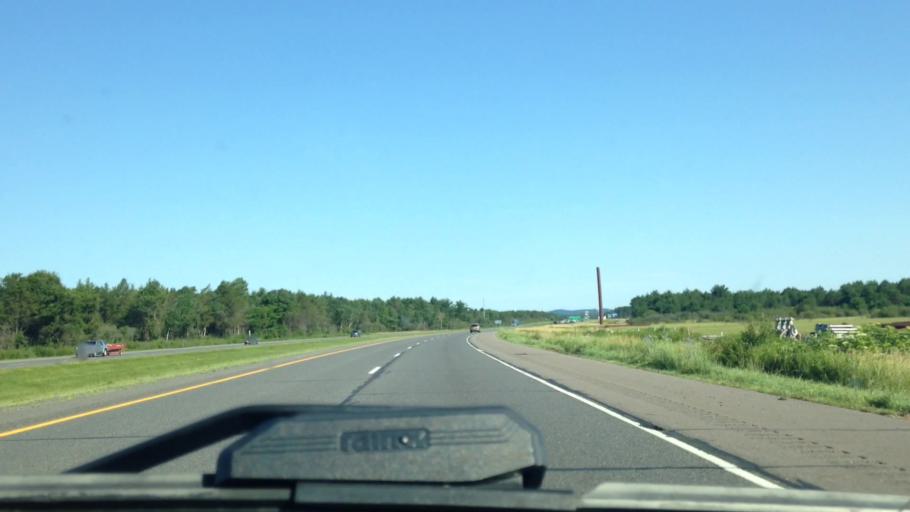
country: US
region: Wisconsin
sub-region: Jackson County
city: Black River Falls
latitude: 44.2791
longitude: -90.8051
